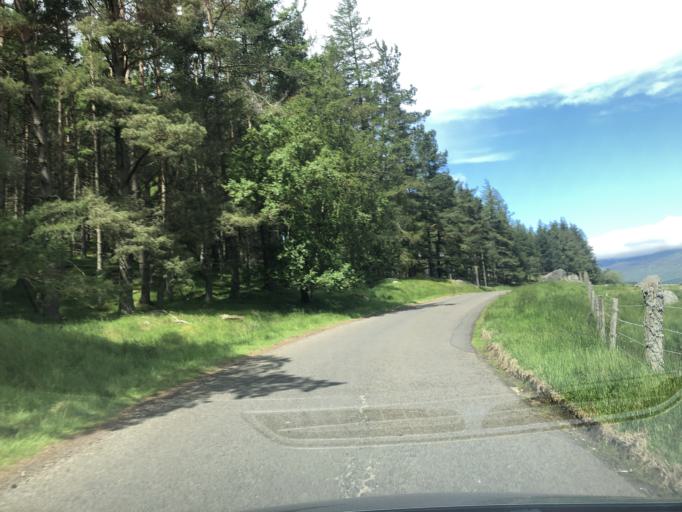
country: GB
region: Scotland
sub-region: Angus
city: Kirriemuir
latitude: 56.7749
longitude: -3.0320
